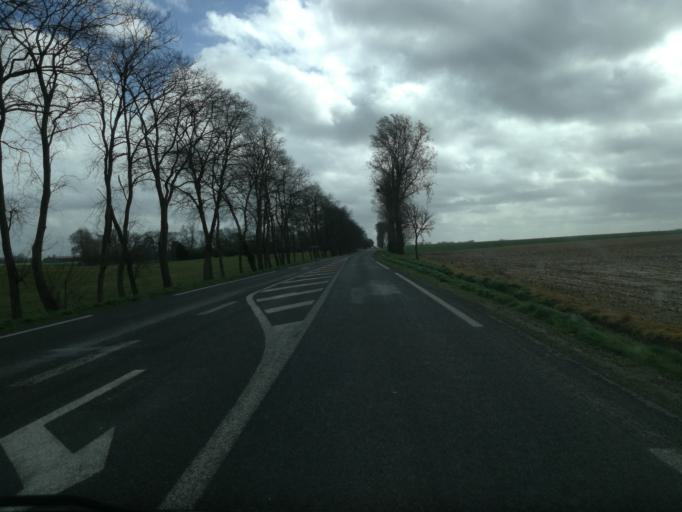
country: FR
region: Haute-Normandie
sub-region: Departement de la Seine-Maritime
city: Fauville-en-Caux
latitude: 49.6450
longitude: 0.6149
